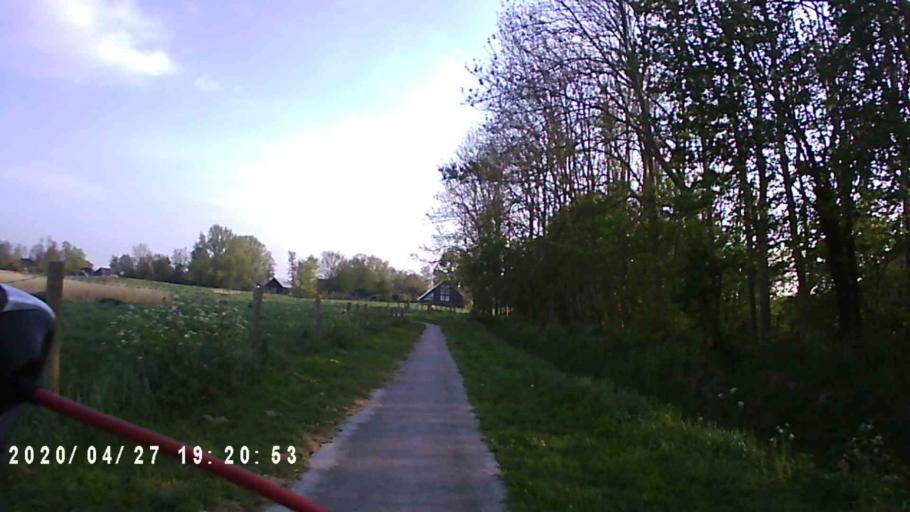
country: NL
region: Groningen
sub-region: Gemeente Winsum
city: Winsum
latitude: 53.4027
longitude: 6.4853
